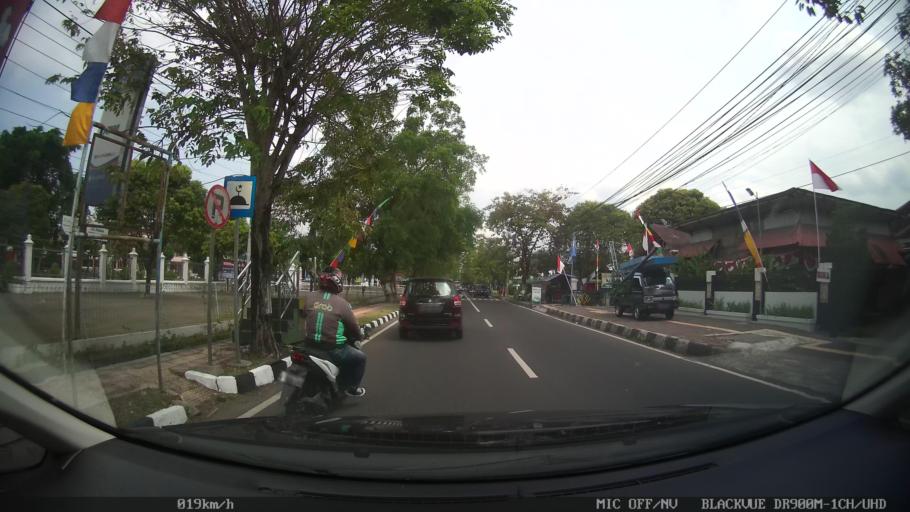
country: ID
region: Daerah Istimewa Yogyakarta
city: Yogyakarta
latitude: -7.7909
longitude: 110.3934
